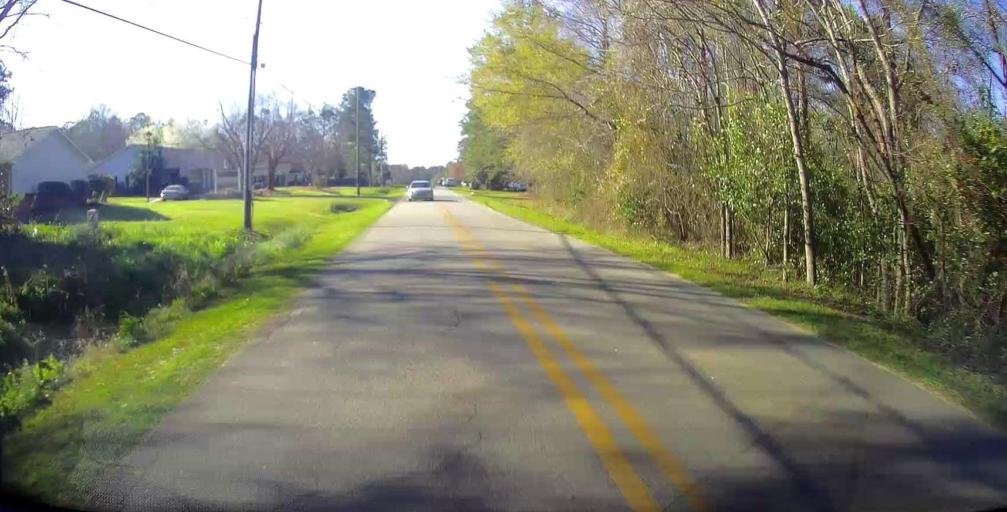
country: US
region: Georgia
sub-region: Macon County
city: Marshallville
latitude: 32.4618
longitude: -83.9417
